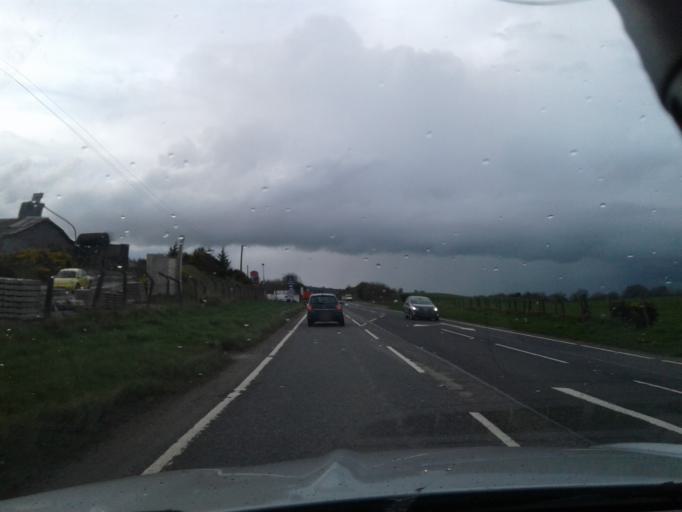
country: GB
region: Northern Ireland
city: Newtownstewart
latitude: 54.7325
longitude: -7.4202
